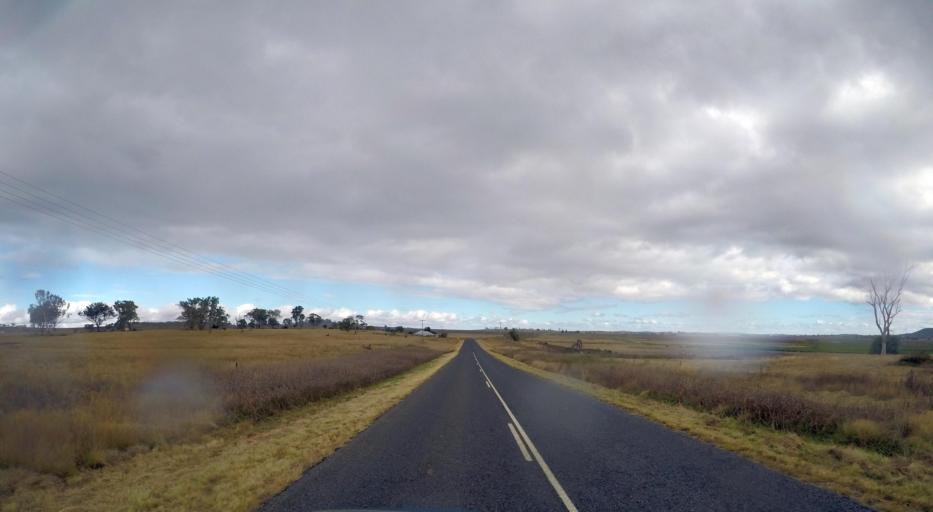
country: AU
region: Queensland
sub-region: Southern Downs
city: Warwick
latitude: -28.0458
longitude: 152.0448
